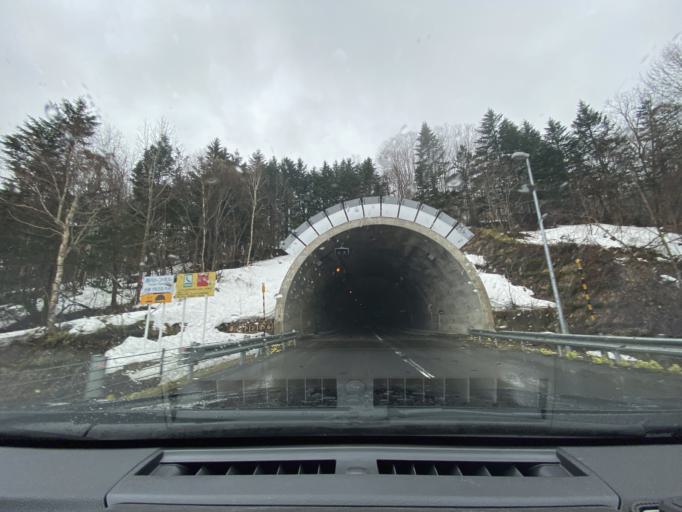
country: JP
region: Hokkaido
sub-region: Asahikawa-shi
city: Asahikawa
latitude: 43.8115
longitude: 142.2457
